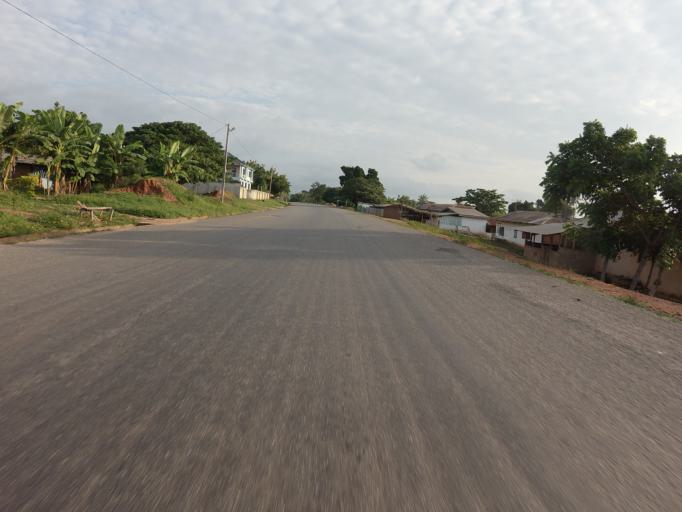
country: GH
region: Volta
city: Kpandu
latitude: 6.8868
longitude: 0.4225
